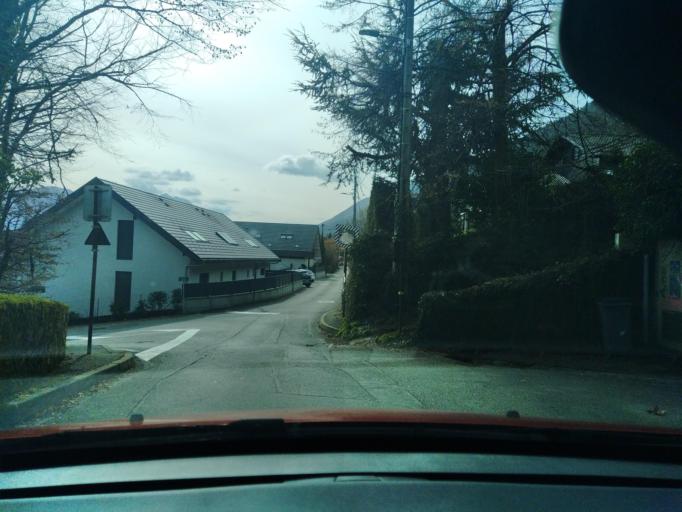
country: FR
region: Rhone-Alpes
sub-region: Departement de la Haute-Savoie
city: Sevrier
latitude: 45.8745
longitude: 6.1396
